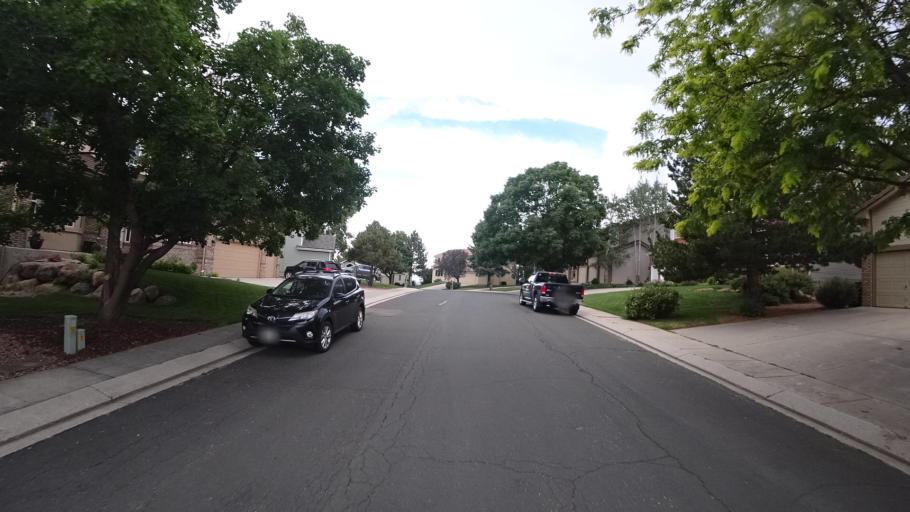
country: US
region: Colorado
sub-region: El Paso County
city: Colorado Springs
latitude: 38.9033
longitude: -104.8372
